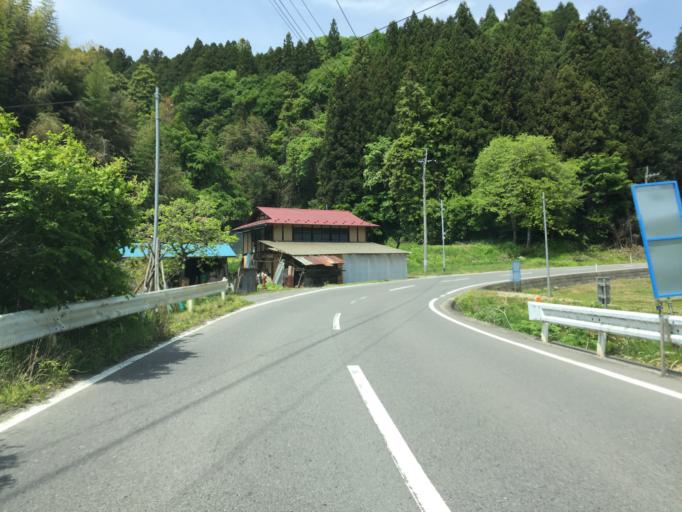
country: JP
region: Fukushima
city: Ishikawa
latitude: 37.1864
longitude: 140.4780
